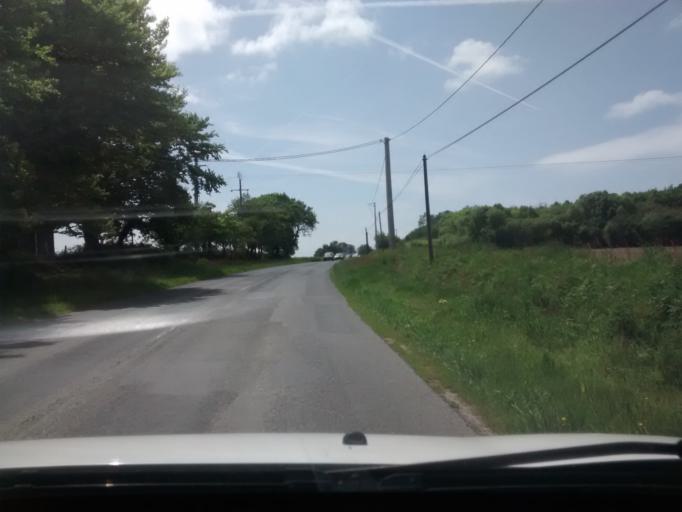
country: FR
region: Brittany
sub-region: Departement des Cotes-d'Armor
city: Saint-Quay-Perros
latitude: 48.7624
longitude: -3.4325
